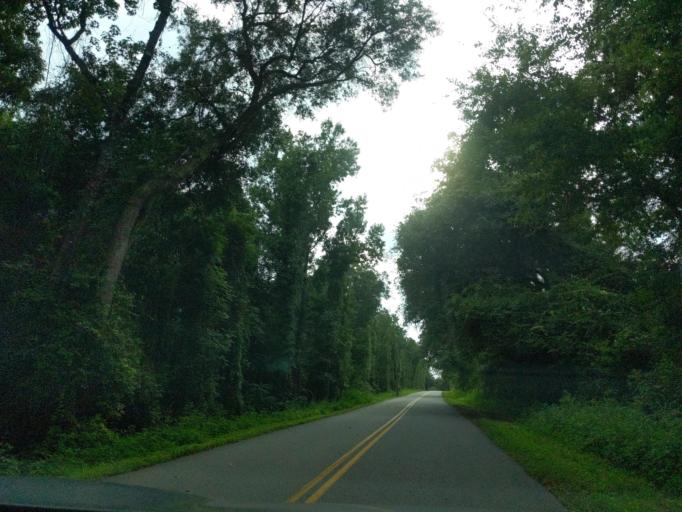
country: US
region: Florida
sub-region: Jefferson County
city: Monticello
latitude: 30.4783
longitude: -83.8894
